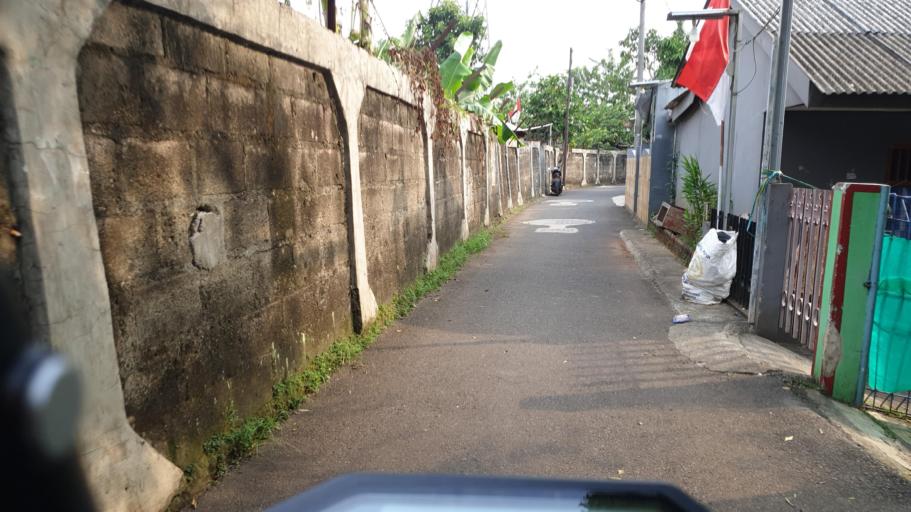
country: ID
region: West Java
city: Depok
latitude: -6.3416
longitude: 106.8285
